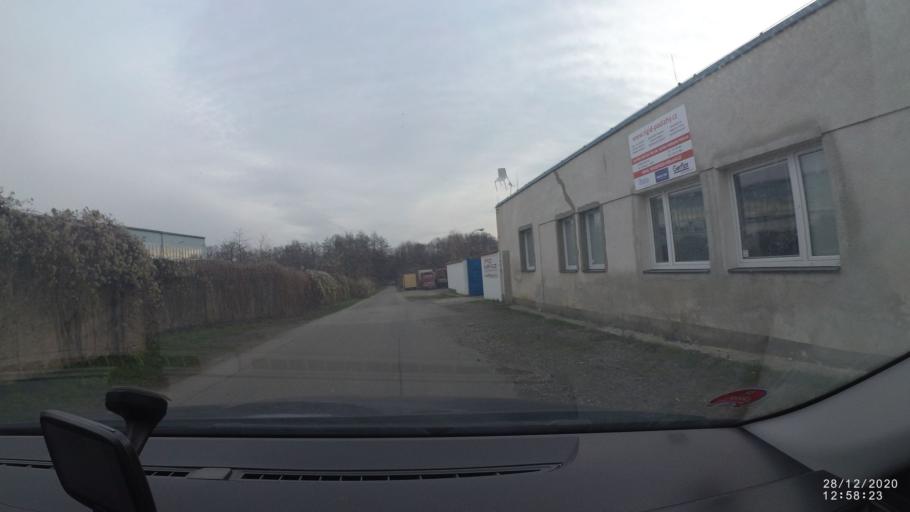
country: CZ
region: Praha
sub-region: Praha 19
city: Satalice
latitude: 50.1508
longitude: 14.5900
